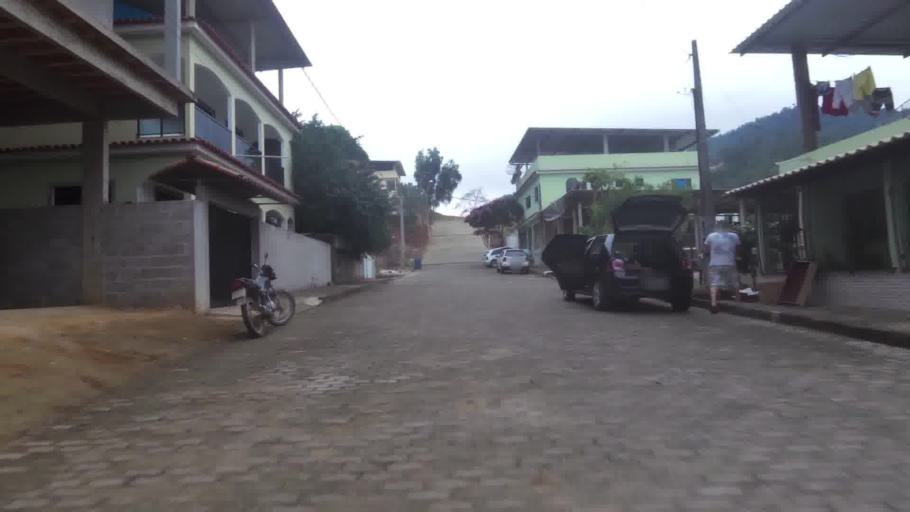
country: BR
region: Espirito Santo
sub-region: Iconha
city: Iconha
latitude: -20.7875
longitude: -40.8170
